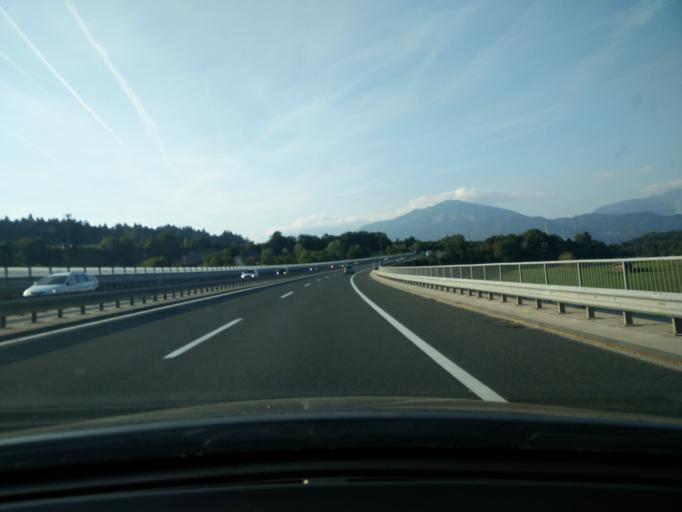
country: SI
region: Naklo
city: Naklo
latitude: 46.2911
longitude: 14.2859
